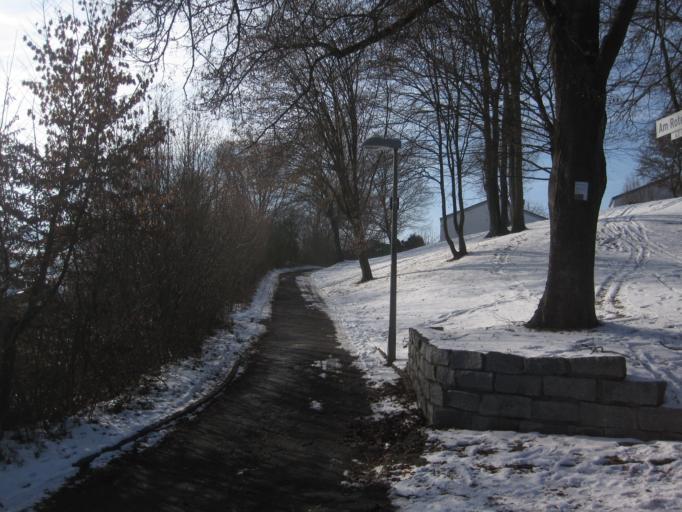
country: DE
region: Baden-Wuerttemberg
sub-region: Tuebingen Region
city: Ulm
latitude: 48.4015
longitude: 9.9365
